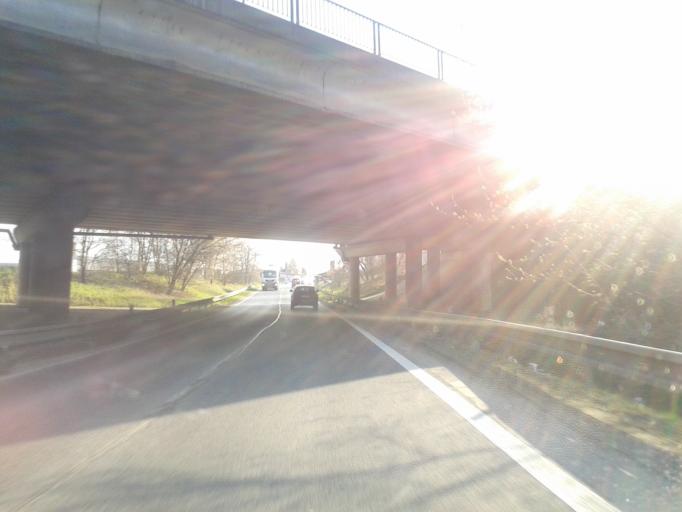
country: CZ
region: Central Bohemia
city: Hostivice
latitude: 50.0492
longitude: 14.2671
